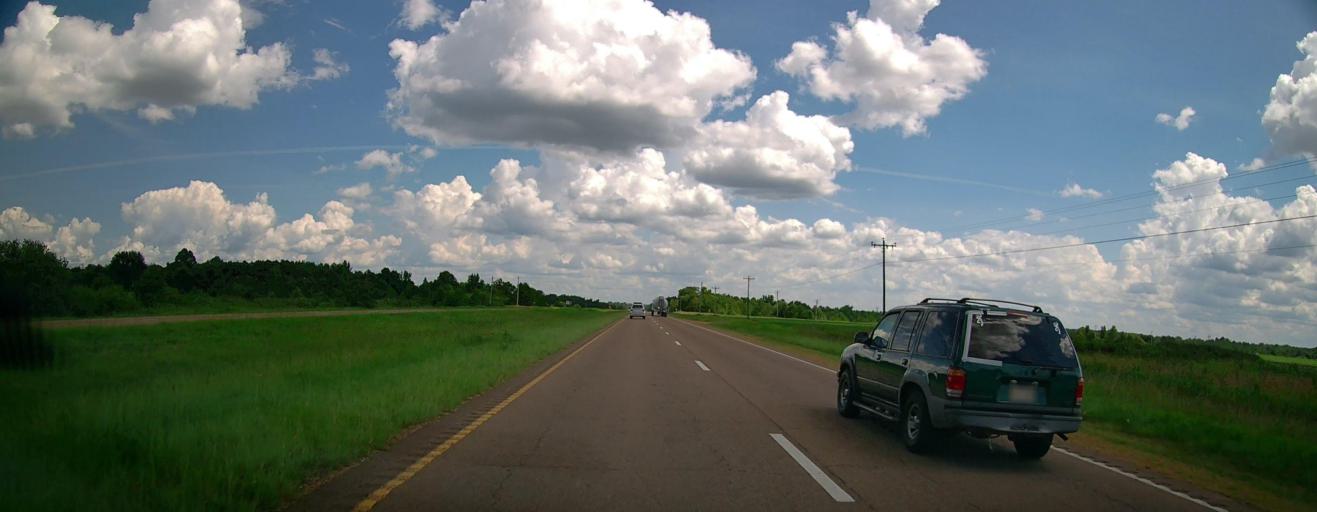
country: US
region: Mississippi
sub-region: Lowndes County
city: Columbus Air Force Base
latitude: 33.6917
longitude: -88.4394
